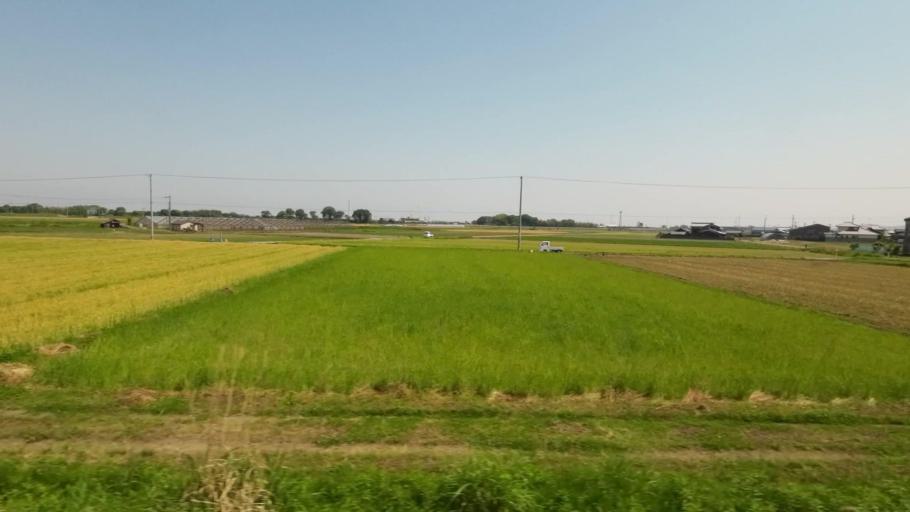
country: JP
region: Ehime
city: Saijo
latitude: 33.8991
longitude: 133.1026
